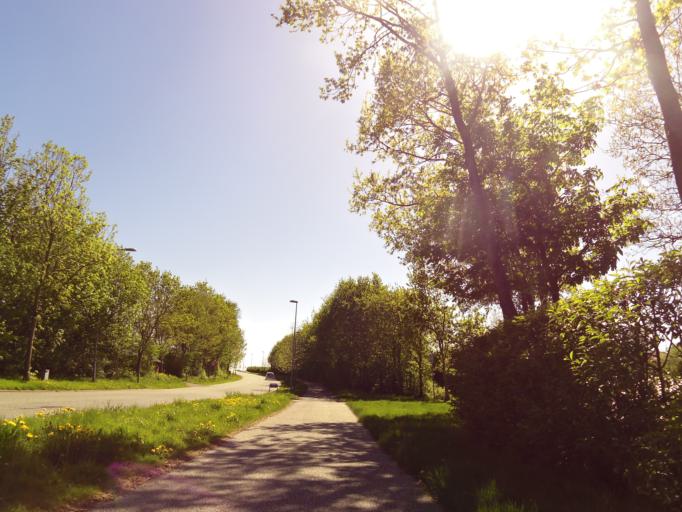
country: DK
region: Central Jutland
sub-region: Holstebro Kommune
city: Vinderup
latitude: 56.4732
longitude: 8.7937
